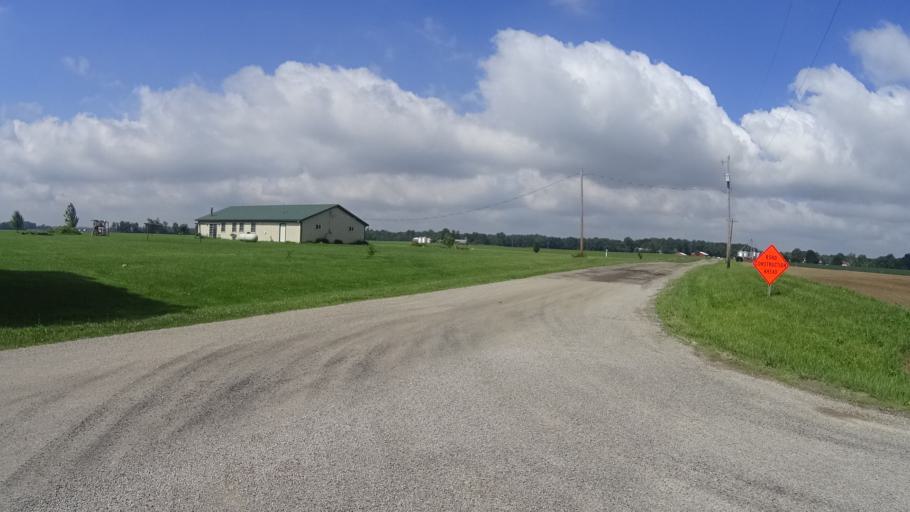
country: US
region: Ohio
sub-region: Huron County
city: Wakeman
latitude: 41.2767
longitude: -82.4125
